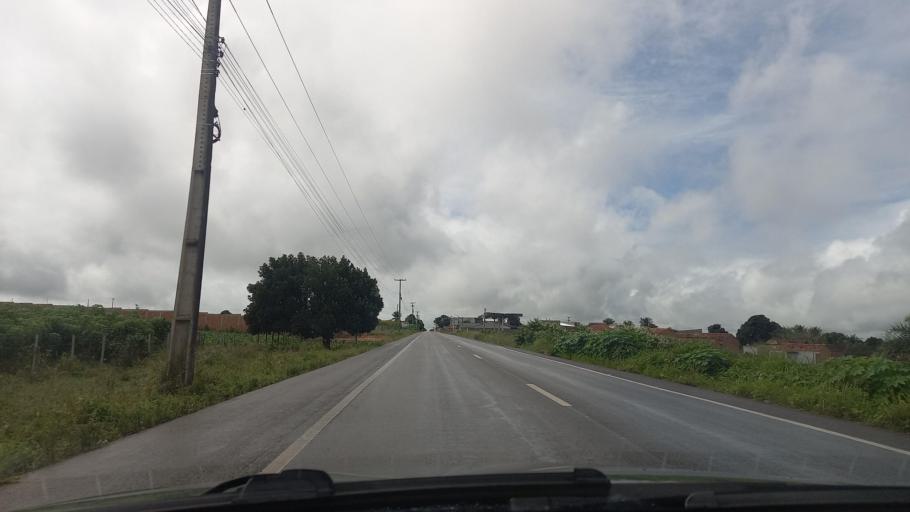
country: BR
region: Alagoas
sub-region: Limoeiro De Anadia
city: Limoeiro de Anadia
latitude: -9.7589
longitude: -36.5641
